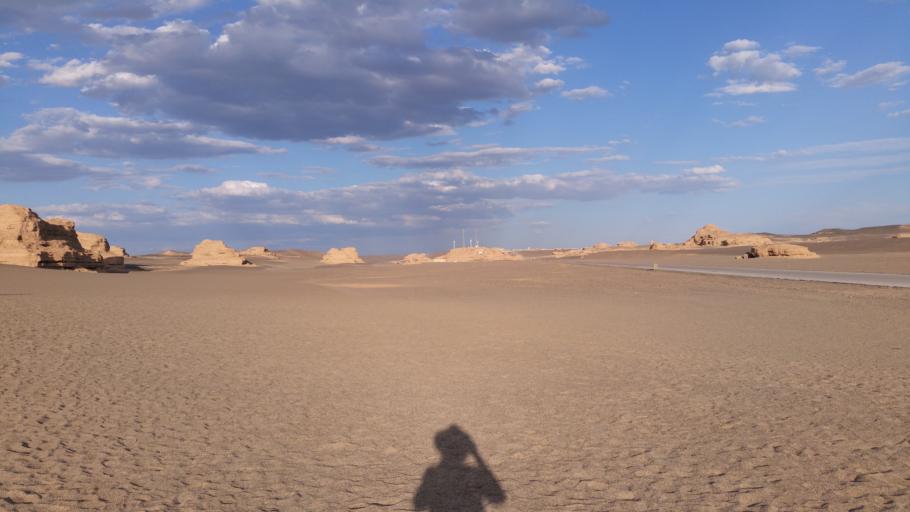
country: CN
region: Heilongjiang Sheng
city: Duobagou
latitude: 40.5166
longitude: 93.2136
